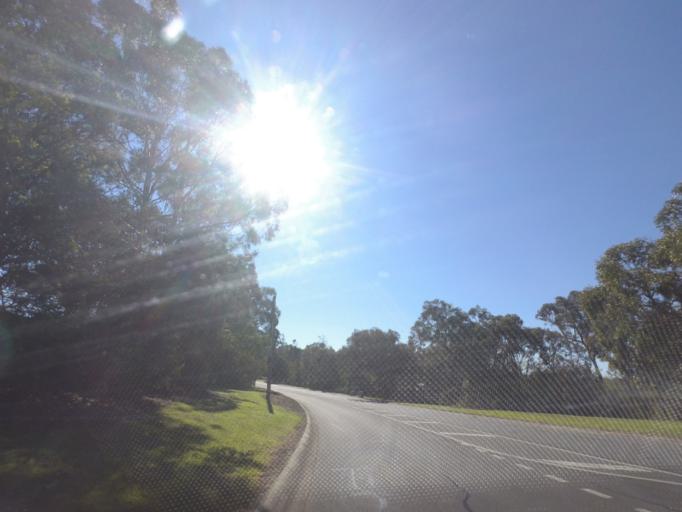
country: AU
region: Victoria
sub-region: Maroondah
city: Croydon Hills
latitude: -37.7701
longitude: 145.2759
